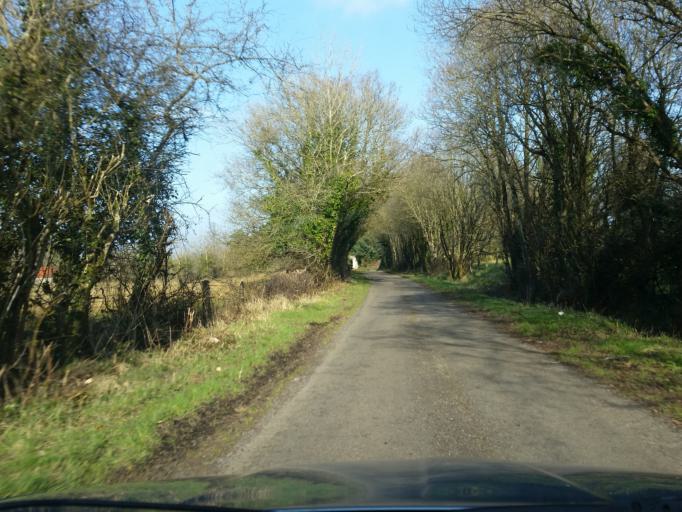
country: IE
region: Ulster
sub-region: County Monaghan
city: Clones
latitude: 54.2281
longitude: -7.2316
